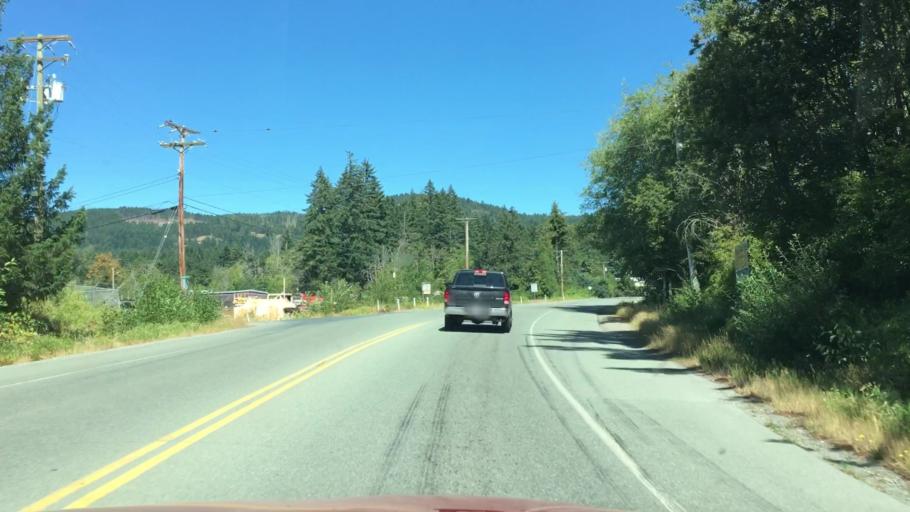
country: CA
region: British Columbia
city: Port Alberni
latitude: 49.2625
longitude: -124.7667
